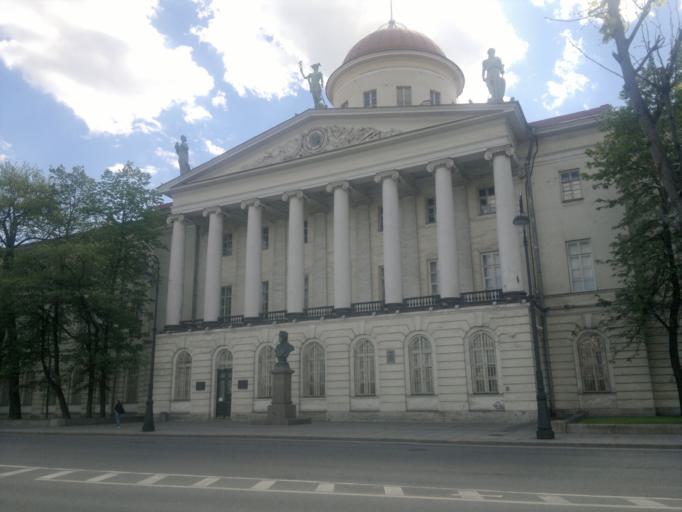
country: RU
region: St.-Petersburg
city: Saint Petersburg
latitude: 59.9453
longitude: 30.3011
